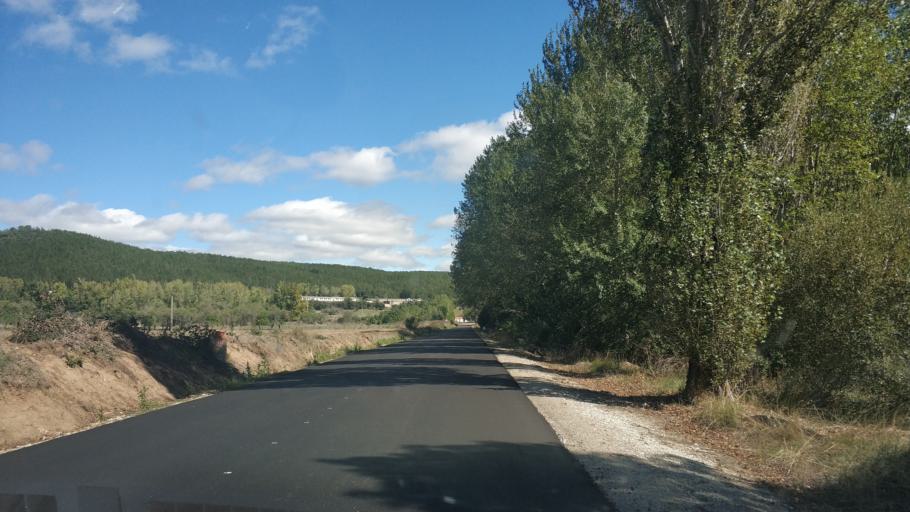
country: ES
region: Castille and Leon
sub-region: Provincia de Burgos
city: Puentedura
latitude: 42.0511
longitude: -3.5646
